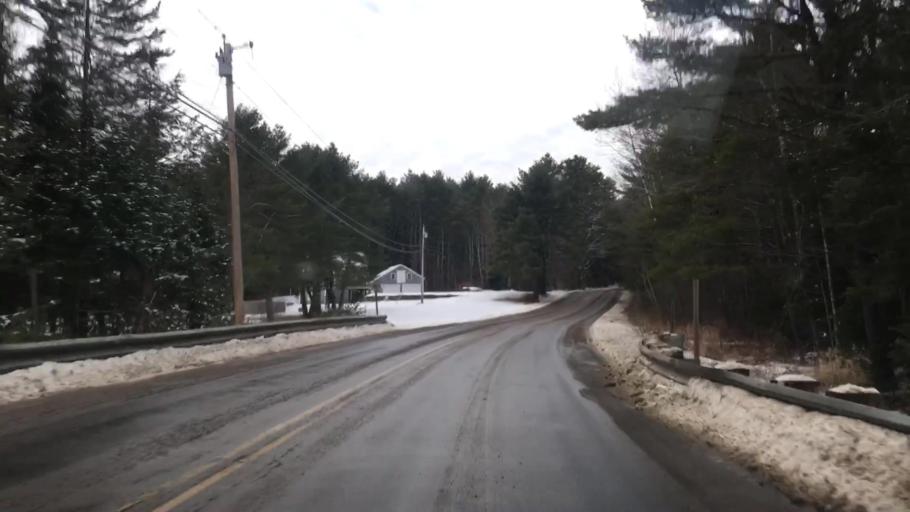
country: US
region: Maine
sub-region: Lincoln County
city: Whitefield
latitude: 44.2413
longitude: -69.6282
